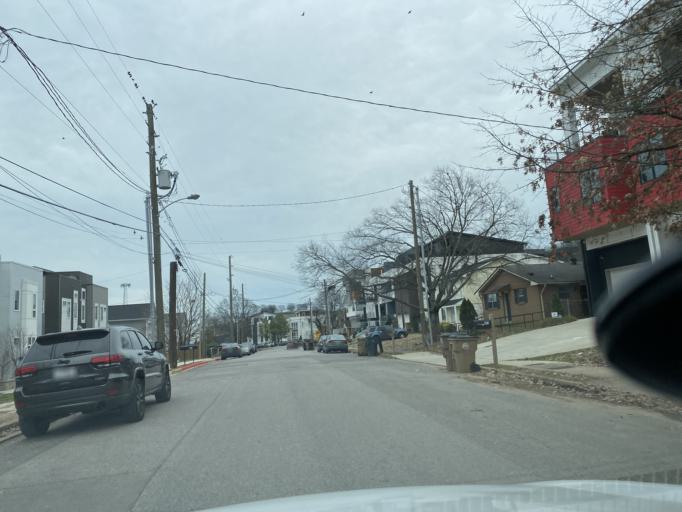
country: US
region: Tennessee
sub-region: Davidson County
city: Nashville
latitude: 36.1462
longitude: -86.7822
